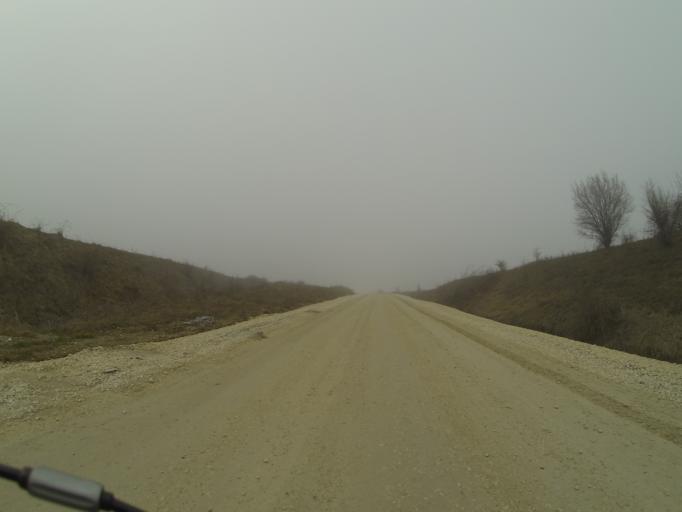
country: RO
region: Mehedinti
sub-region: Comuna Balacita
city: Gvardinita
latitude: 44.4114
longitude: 23.1420
